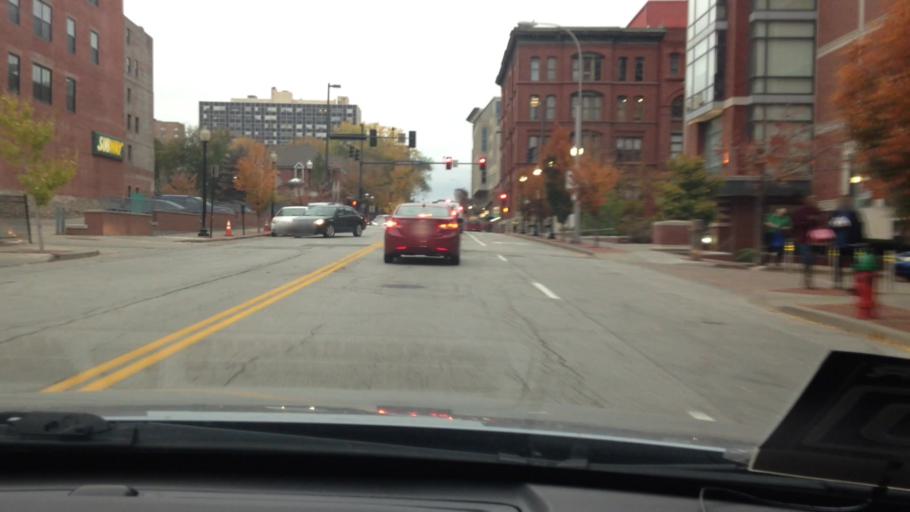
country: US
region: Missouri
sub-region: Jackson County
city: Kansas City
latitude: 39.1037
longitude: -94.5872
